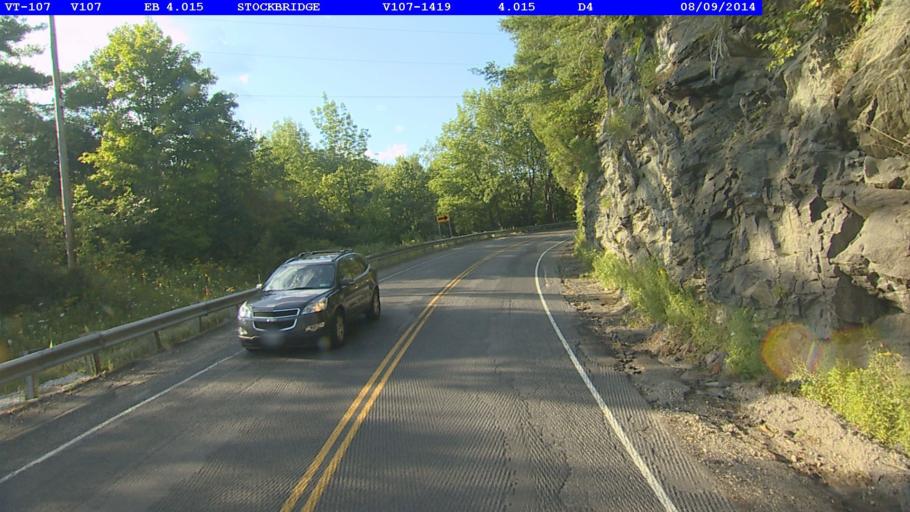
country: US
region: Vermont
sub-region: Orange County
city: Randolph
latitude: 43.7738
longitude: -72.7039
